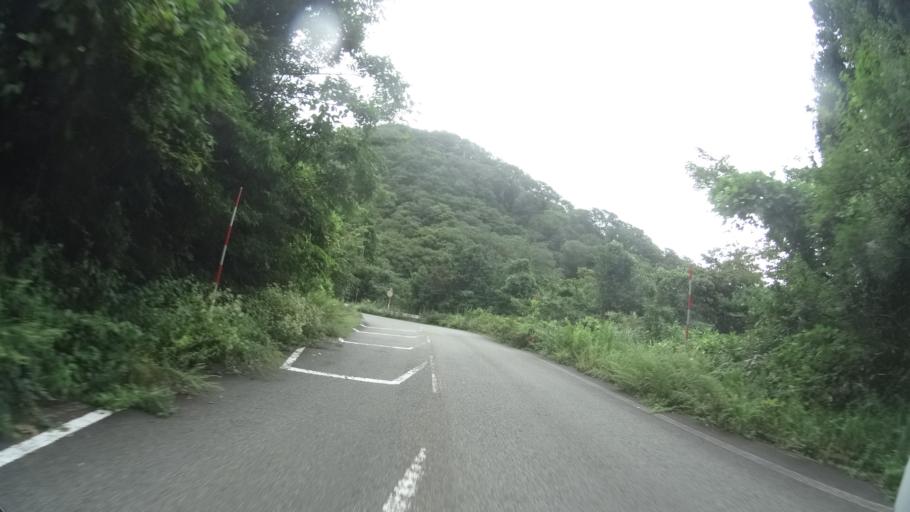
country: JP
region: Tottori
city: Kurayoshi
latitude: 35.4017
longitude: 134.0068
